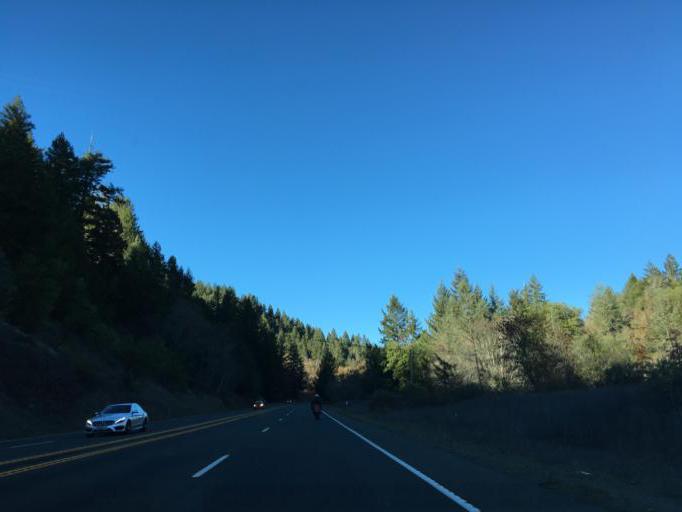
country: US
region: California
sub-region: Mendocino County
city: Laytonville
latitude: 39.5910
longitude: -123.4526
